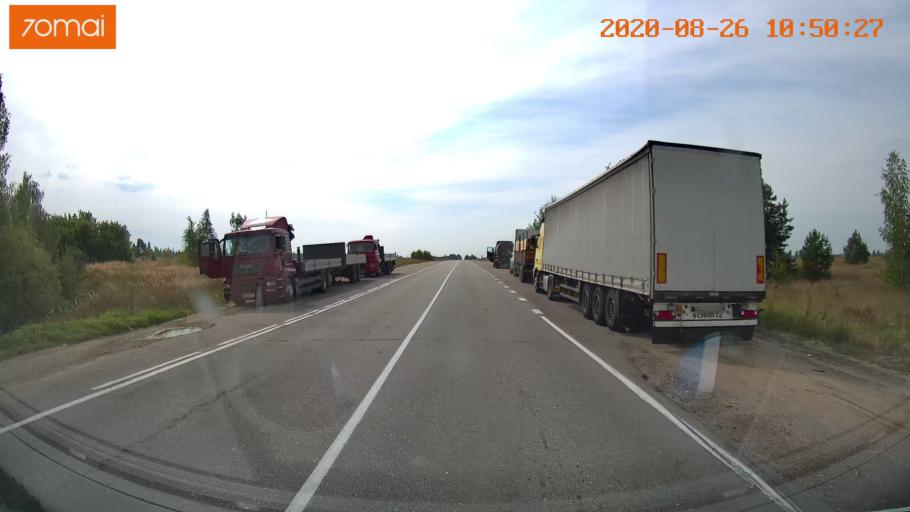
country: RU
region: Rjazan
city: Lashma
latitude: 54.6868
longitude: 41.1564
